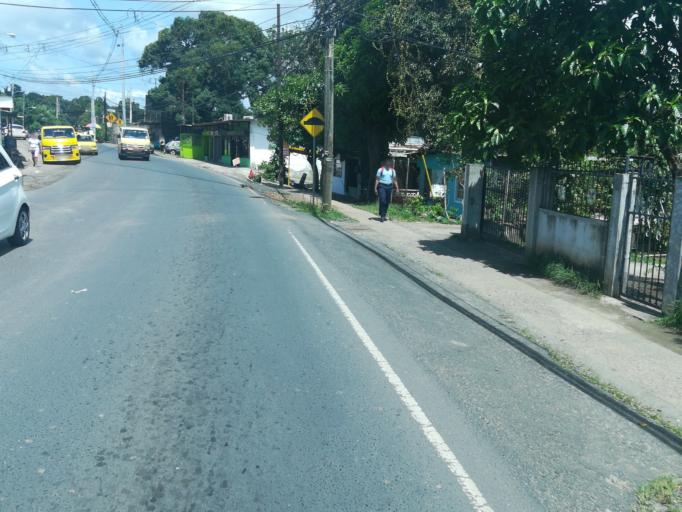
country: PA
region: Panama
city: Tocumen
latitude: 9.0817
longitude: -79.4046
